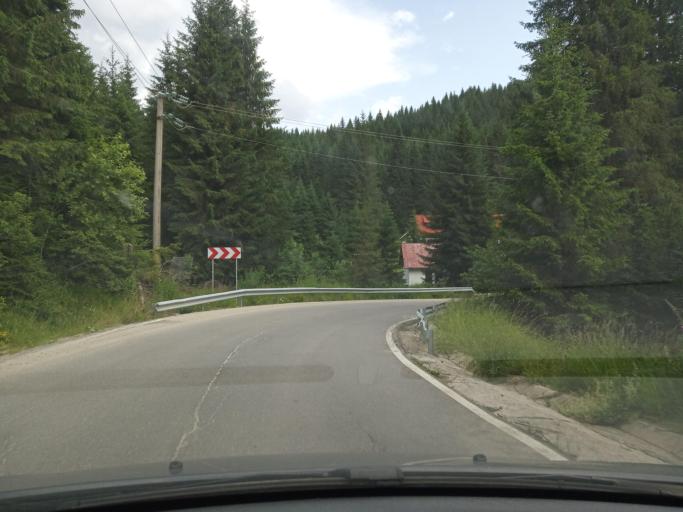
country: RO
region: Dambovita
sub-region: Comuna Moroeni
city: Glod
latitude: 45.3348
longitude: 25.4297
